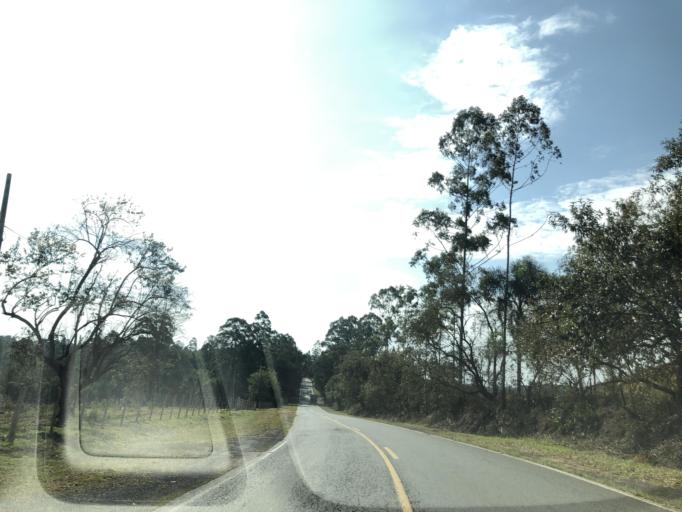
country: BR
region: Sao Paulo
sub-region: Pilar Do Sul
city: Pilar do Sul
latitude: -23.8192
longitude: -47.6805
